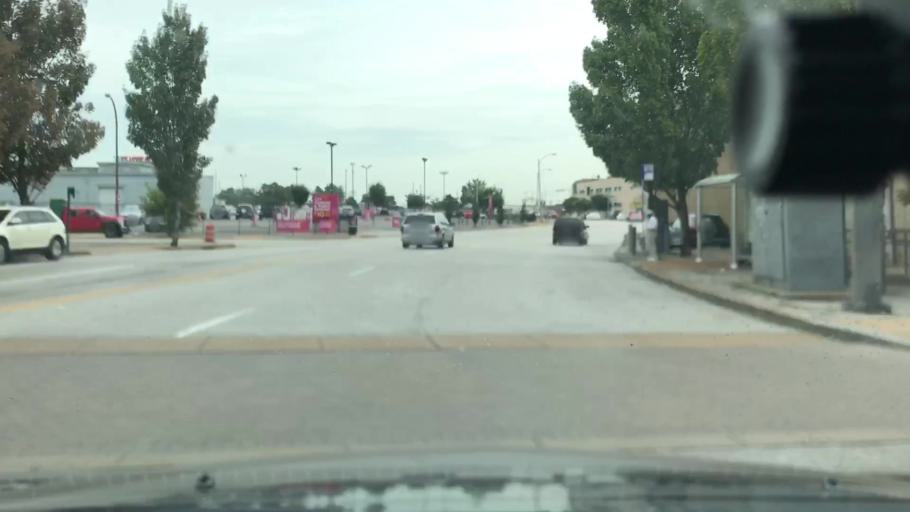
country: US
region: Missouri
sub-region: City of Saint Louis
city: St. Louis
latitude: 38.6324
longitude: -90.1995
